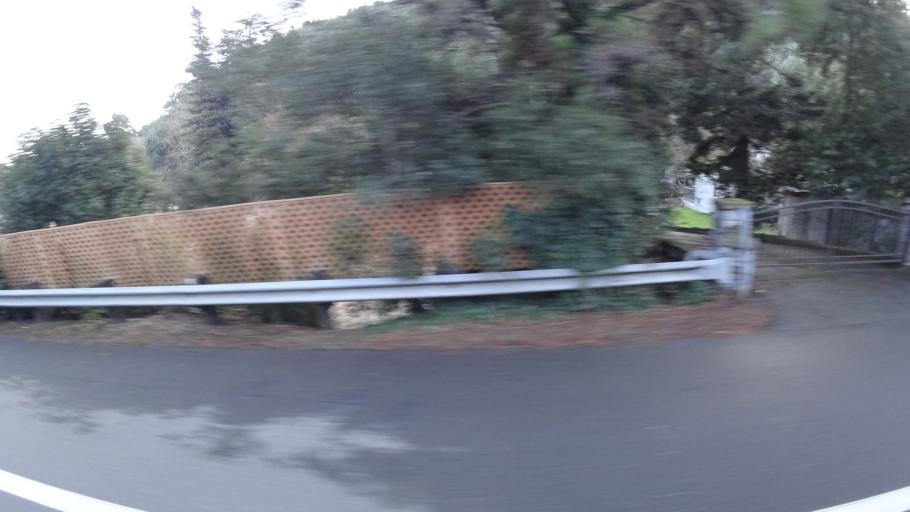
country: US
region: California
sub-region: Alameda County
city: Fairview
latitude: 37.6989
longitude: -122.0294
